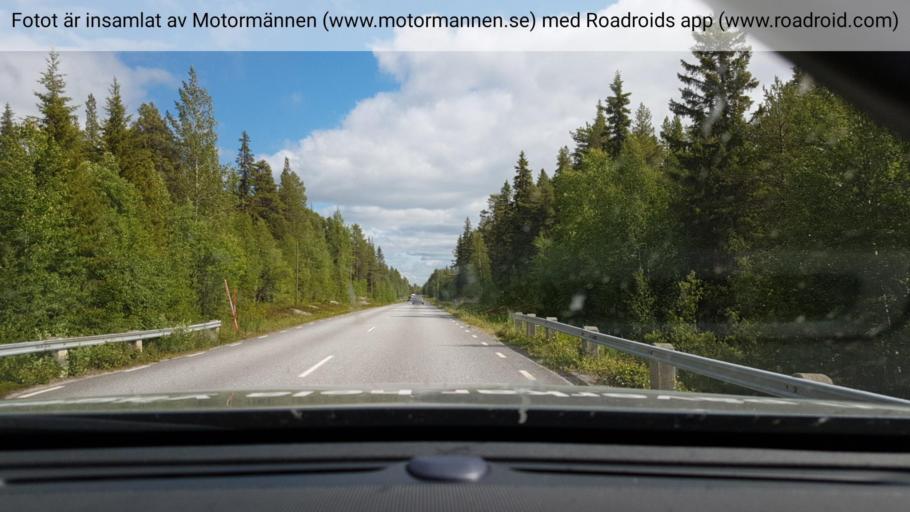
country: SE
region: Vaesterbotten
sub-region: Sorsele Kommun
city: Sorsele
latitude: 65.6680
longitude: 17.3910
